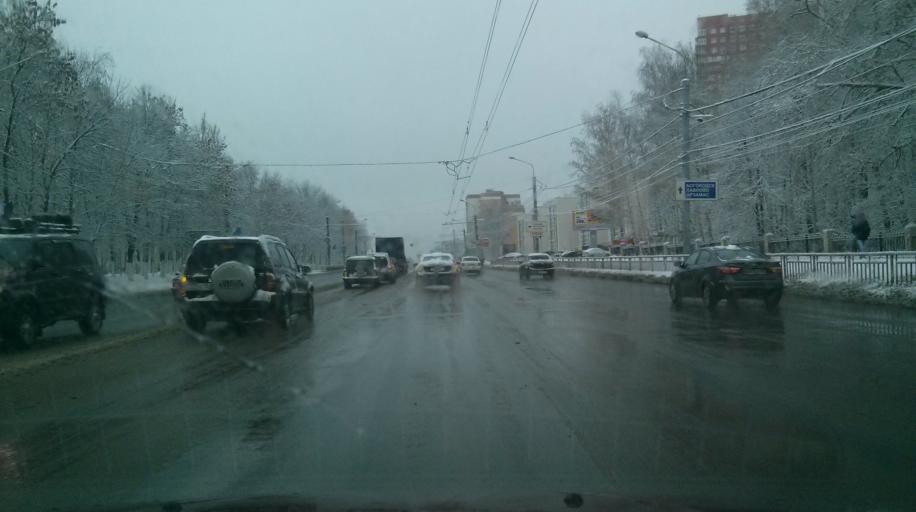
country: RU
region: Nizjnij Novgorod
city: Nizhniy Novgorod
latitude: 56.2393
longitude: 43.9597
